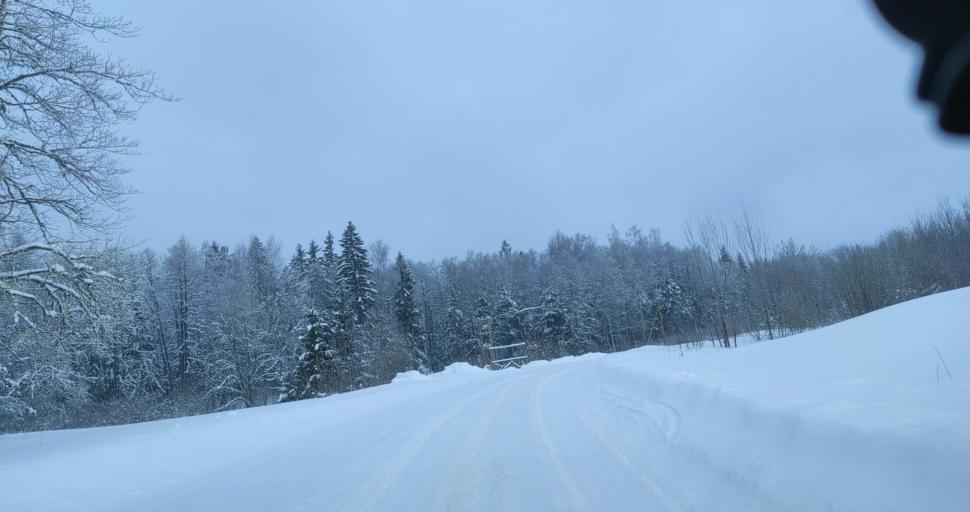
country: LV
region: Vecpiebalga
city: Vecpiebalga
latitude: 56.8707
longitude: 25.9716
